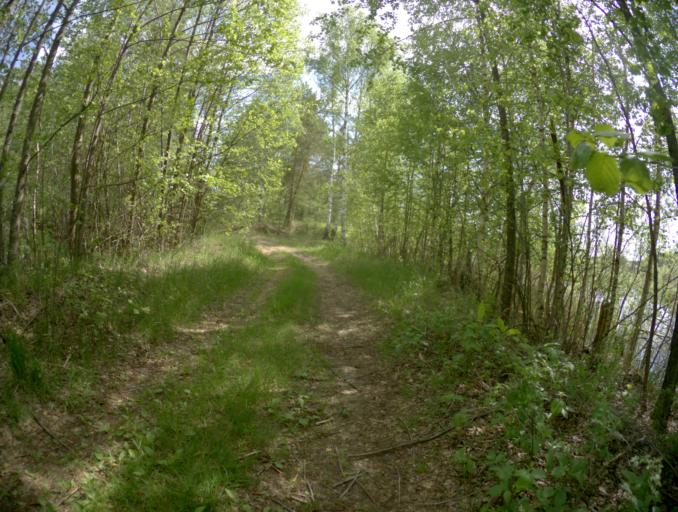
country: RU
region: Vladimir
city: Ivanishchi
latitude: 55.6831
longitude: 40.3983
